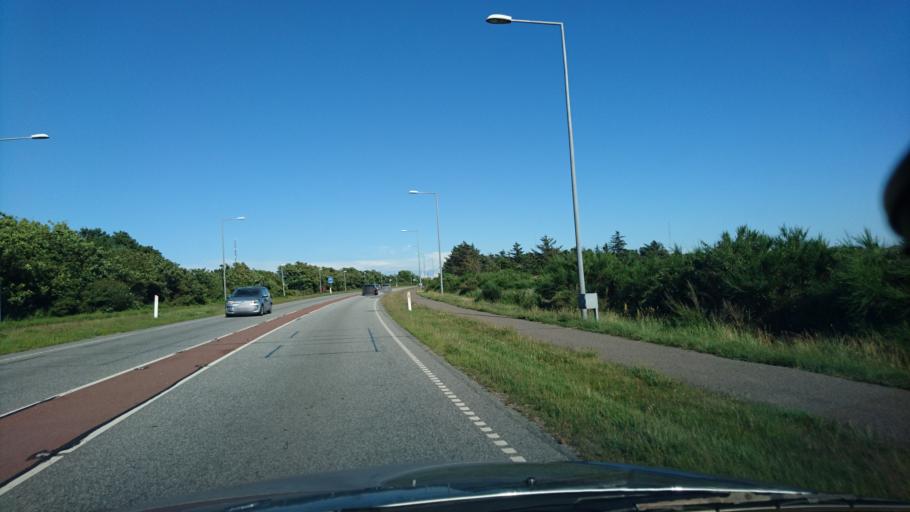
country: DK
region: North Denmark
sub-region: Frederikshavn Kommune
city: Skagen
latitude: 57.7266
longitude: 10.5543
